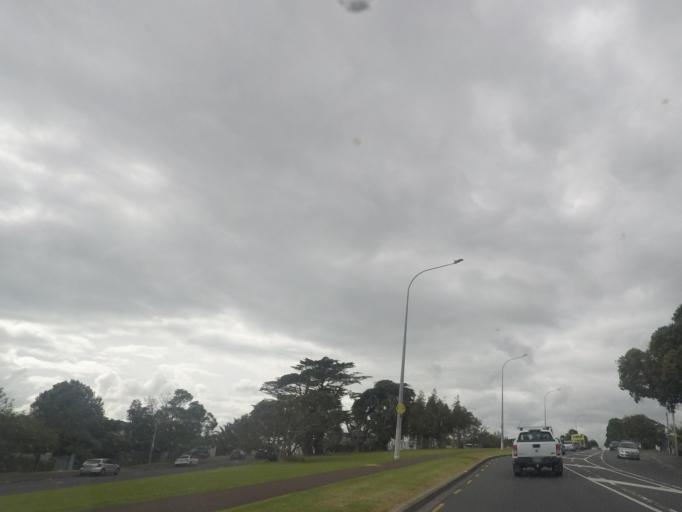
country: NZ
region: Auckland
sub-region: Auckland
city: Tamaki
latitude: -36.8651
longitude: 174.8435
